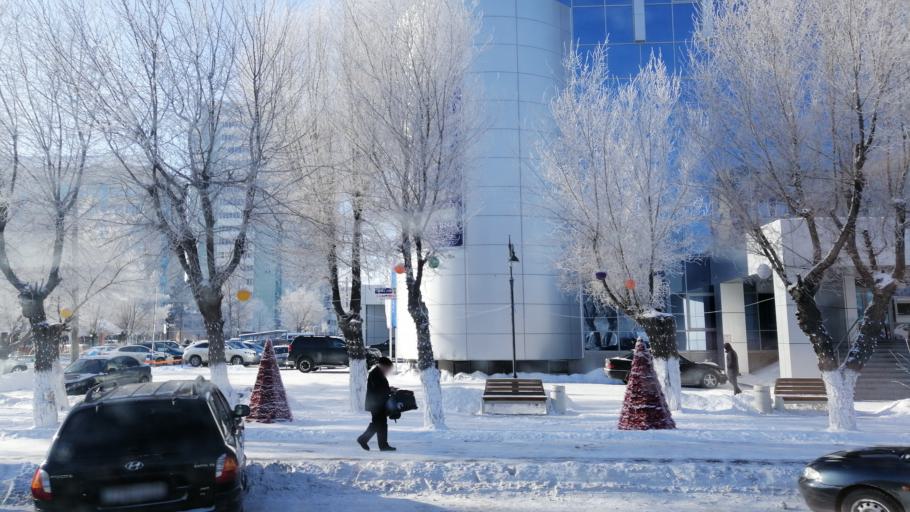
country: KZ
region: Aqtoebe
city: Aqtobe
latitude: 50.2990
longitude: 57.1555
